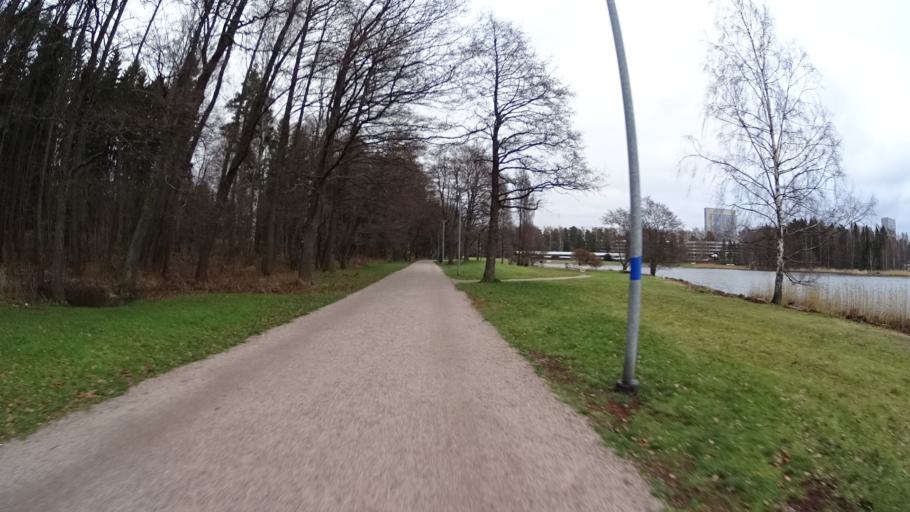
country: FI
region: Uusimaa
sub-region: Helsinki
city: Otaniemi
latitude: 60.1757
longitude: 24.8184
